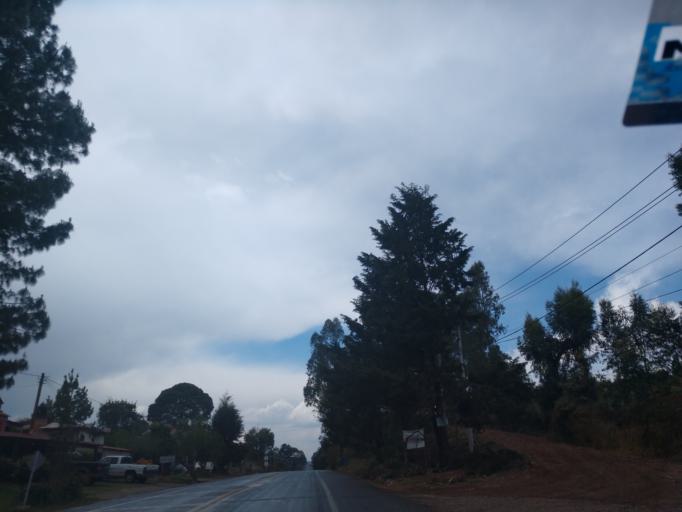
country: MX
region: Jalisco
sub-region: Mazamitla
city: Mazamitla
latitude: 19.9466
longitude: -103.0684
